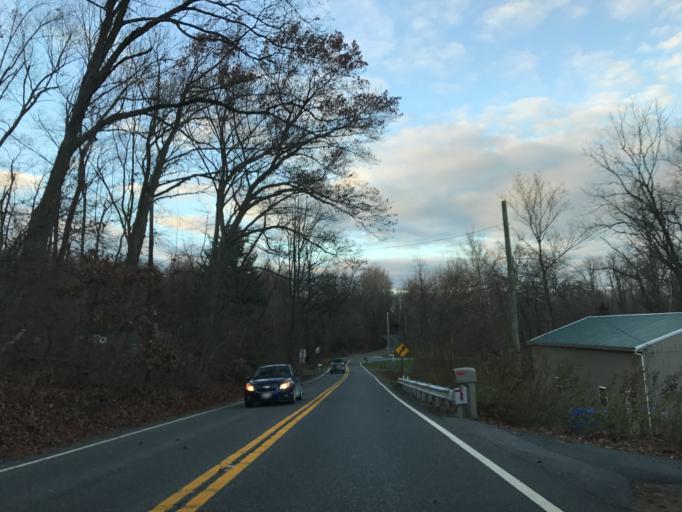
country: US
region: Pennsylvania
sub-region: York County
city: Susquehanna Trails
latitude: 39.7201
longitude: -76.2766
